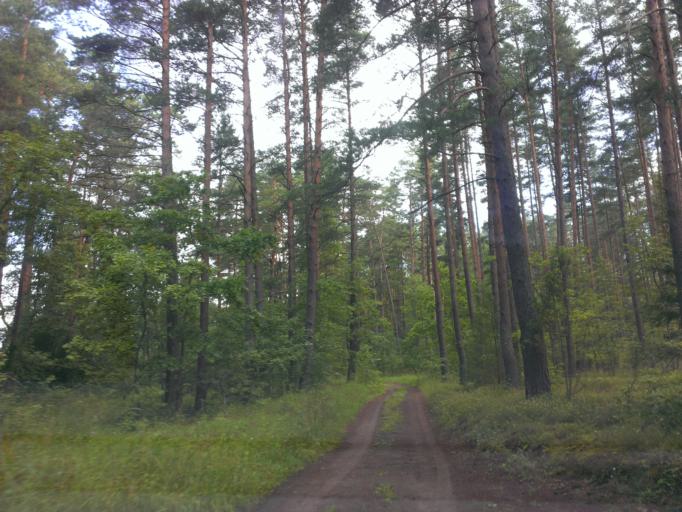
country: LV
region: Incukalns
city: Vangazi
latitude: 57.1025
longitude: 24.5303
